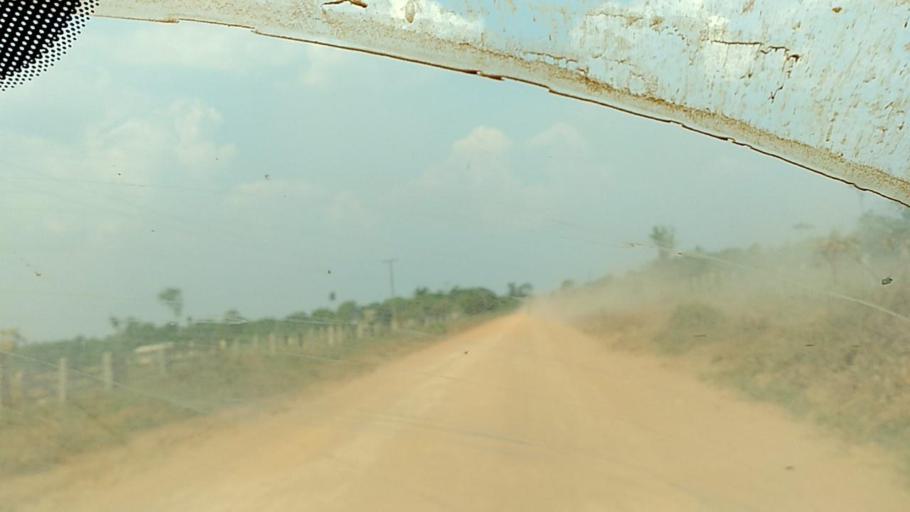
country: BR
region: Rondonia
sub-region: Porto Velho
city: Porto Velho
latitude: -8.6831
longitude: -63.2110
